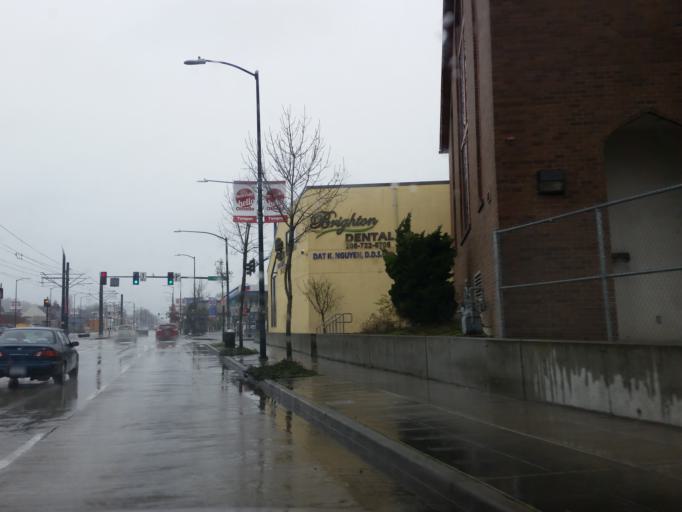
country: US
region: Washington
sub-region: King County
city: Riverton
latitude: 47.5419
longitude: -122.2834
